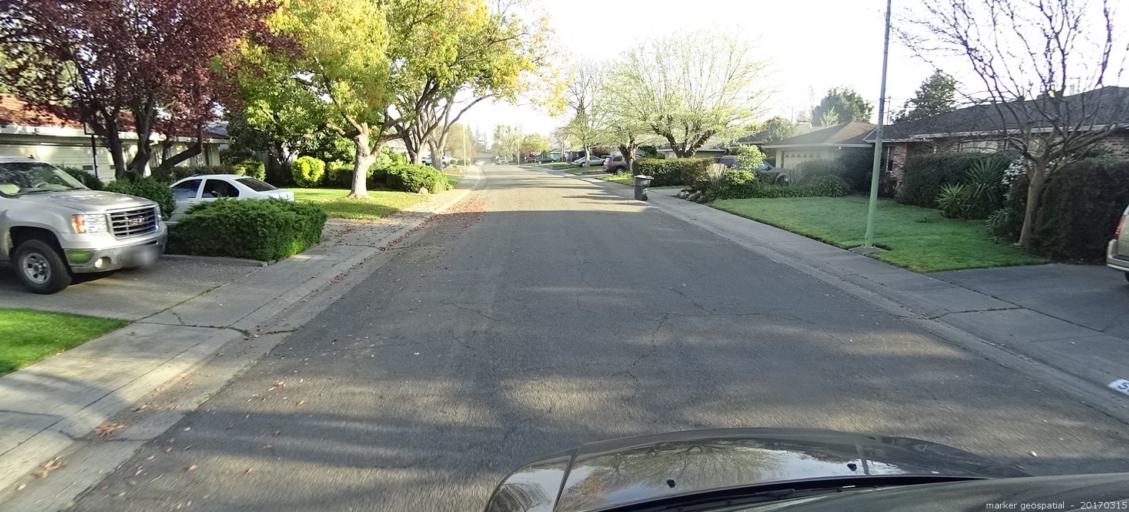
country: US
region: California
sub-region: Sacramento County
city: Parkway
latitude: 38.5184
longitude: -121.5076
